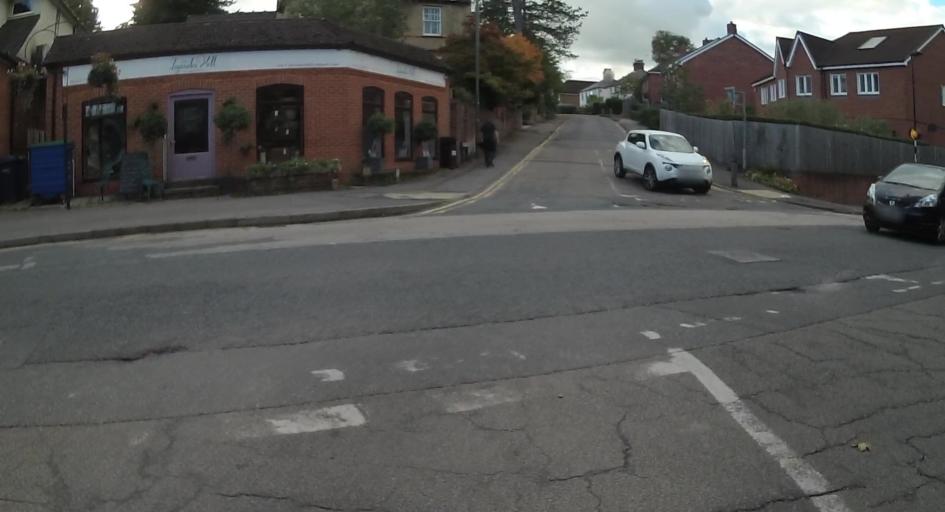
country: GB
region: England
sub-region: Surrey
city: Farnham
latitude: 51.1966
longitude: -0.7902
